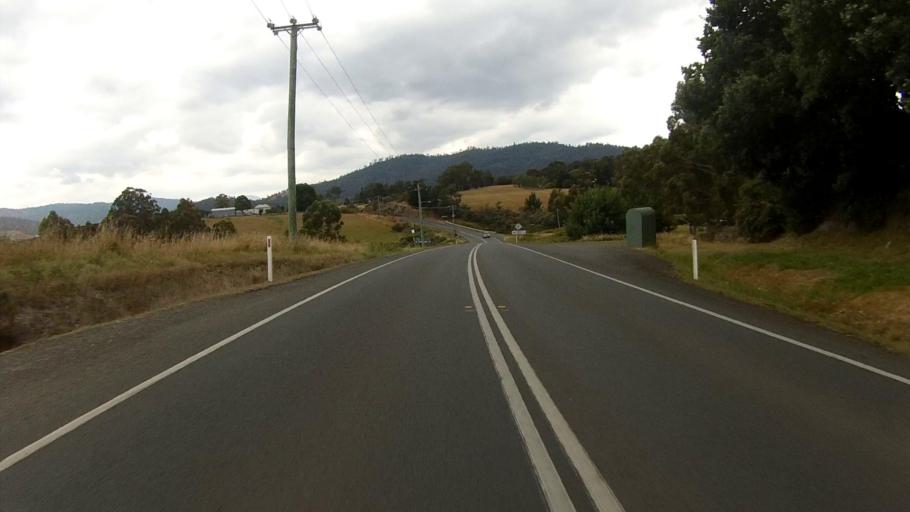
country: AU
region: Tasmania
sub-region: Huon Valley
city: Franklin
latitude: -43.1152
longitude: 147.0356
